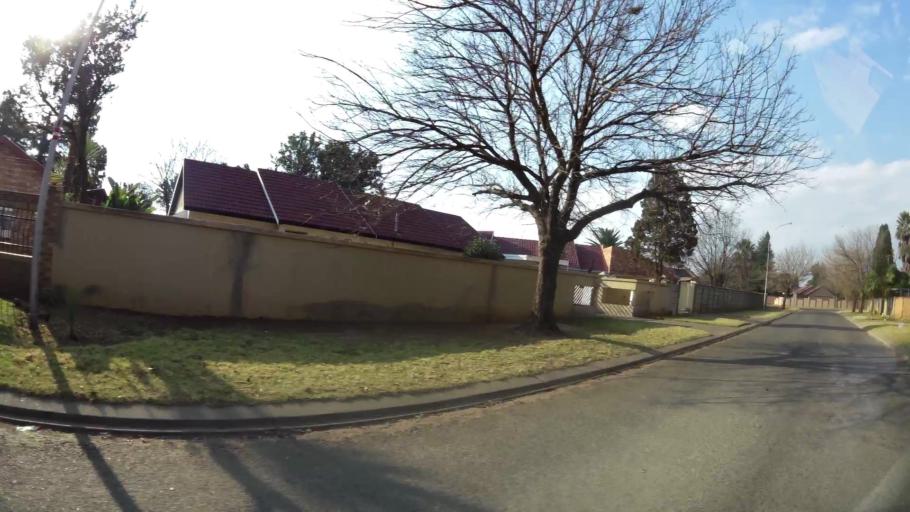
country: ZA
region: Gauteng
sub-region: Ekurhuleni Metropolitan Municipality
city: Benoni
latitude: -26.1265
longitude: 28.3690
